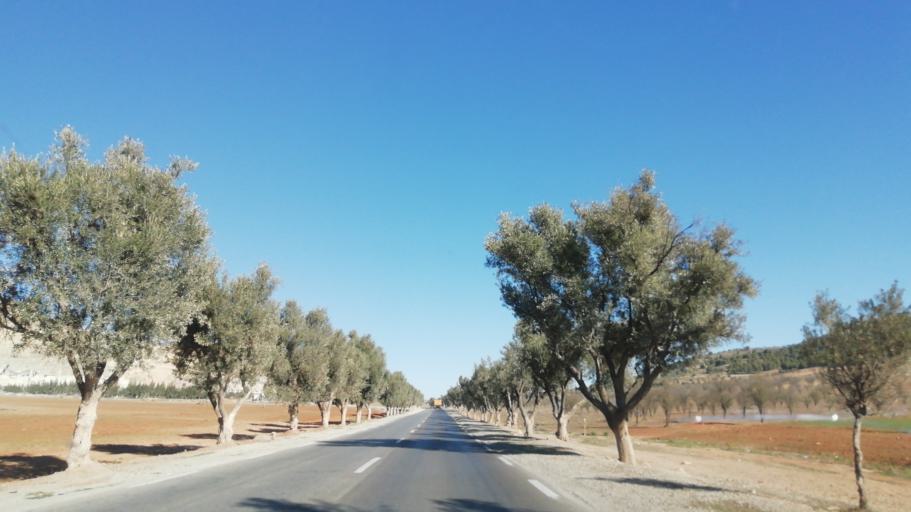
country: DZ
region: Mascara
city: Mascara
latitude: 35.2366
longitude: 0.1169
